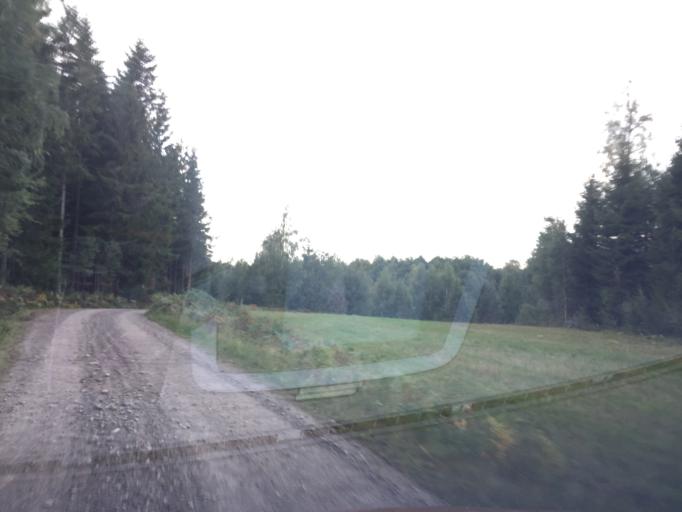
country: SE
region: Soedermanland
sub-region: Vingakers Kommun
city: Vingaker
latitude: 58.9851
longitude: 15.7254
